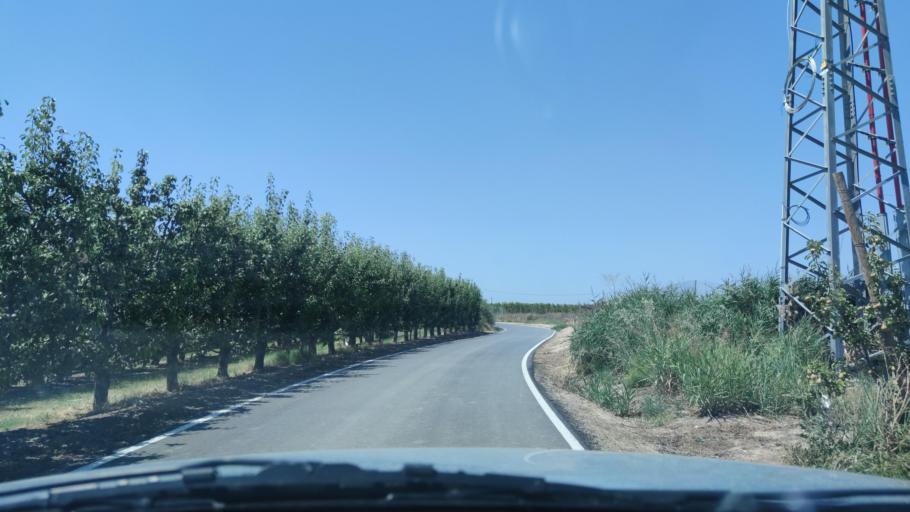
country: ES
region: Catalonia
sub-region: Provincia de Lleida
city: Alpicat
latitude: 41.6589
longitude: 0.5718
